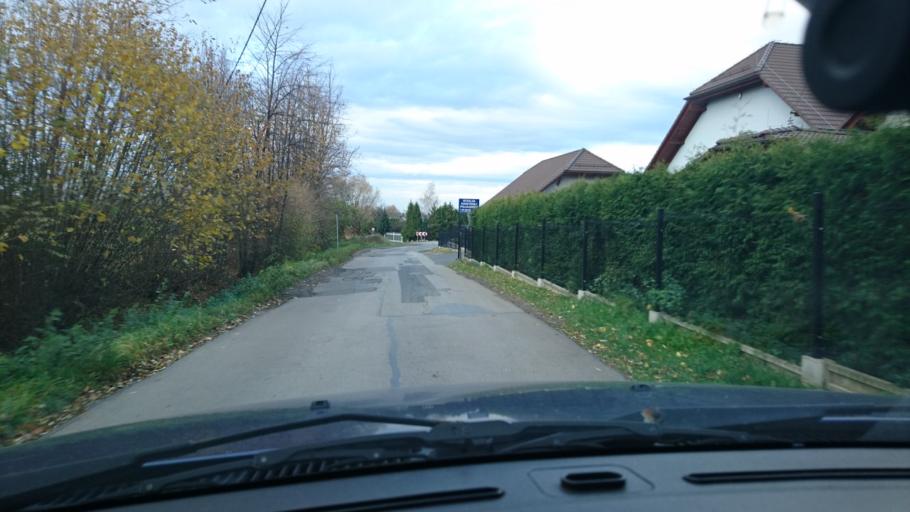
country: PL
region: Silesian Voivodeship
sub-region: Powiat bielski
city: Kozy
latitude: 49.8398
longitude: 19.1167
